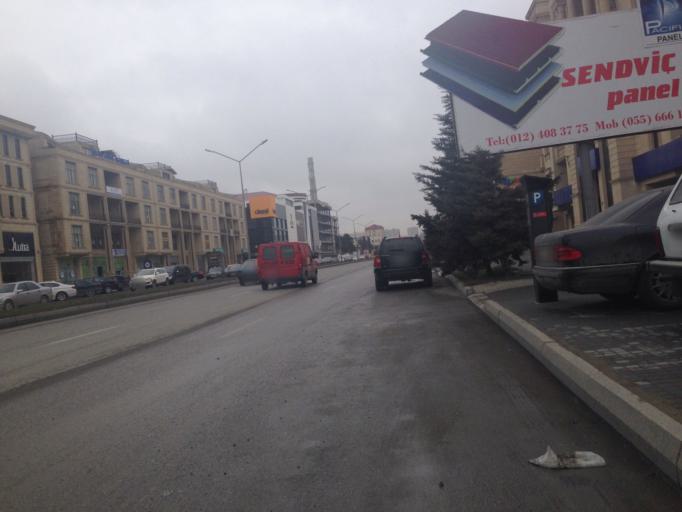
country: AZ
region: Baki
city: Baku
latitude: 40.4124
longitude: 49.8616
